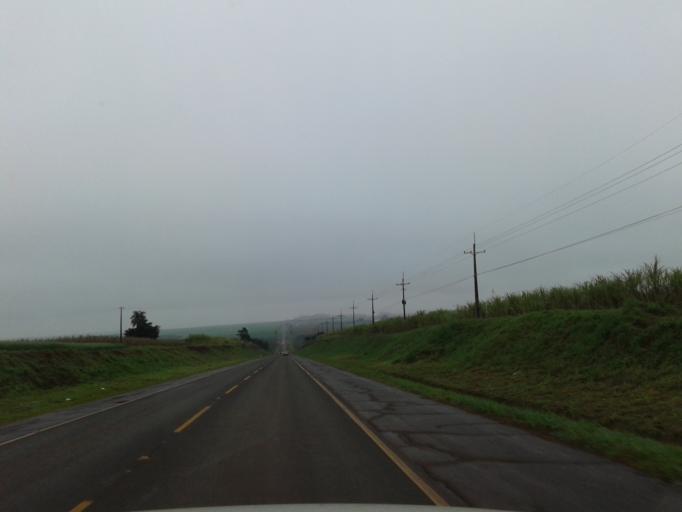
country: PY
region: Alto Parana
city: Naranjal
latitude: -25.9177
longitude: -55.1151
